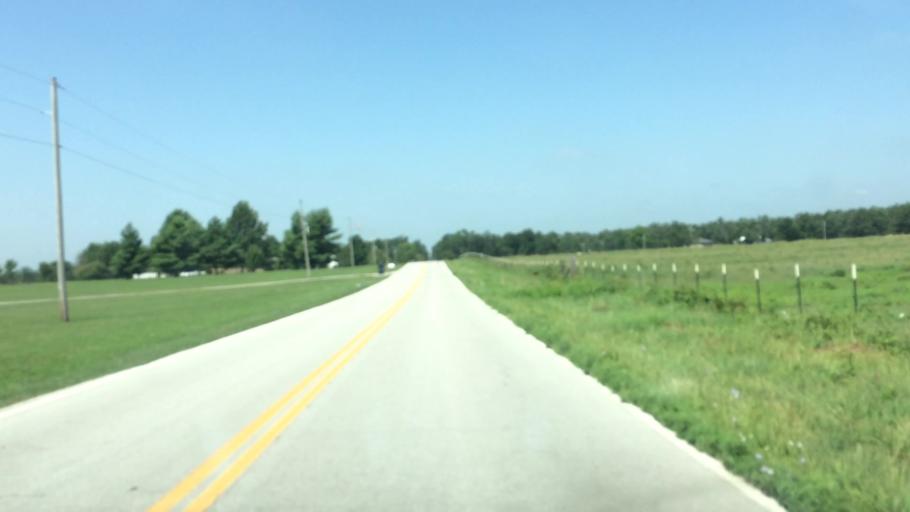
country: US
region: Missouri
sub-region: Greene County
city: Strafford
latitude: 37.2717
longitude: -93.1704
